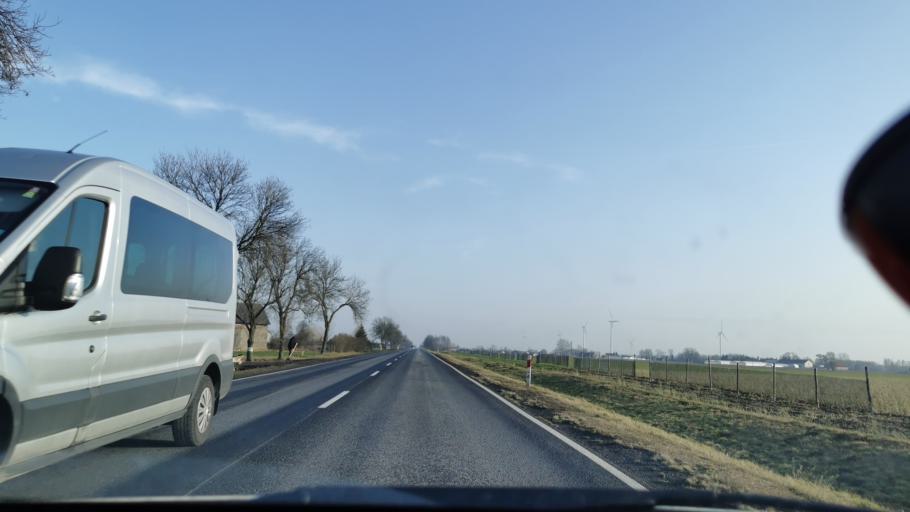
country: PL
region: Lodz Voivodeship
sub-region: Powiat sieradzki
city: Blaszki
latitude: 51.6716
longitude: 18.3700
